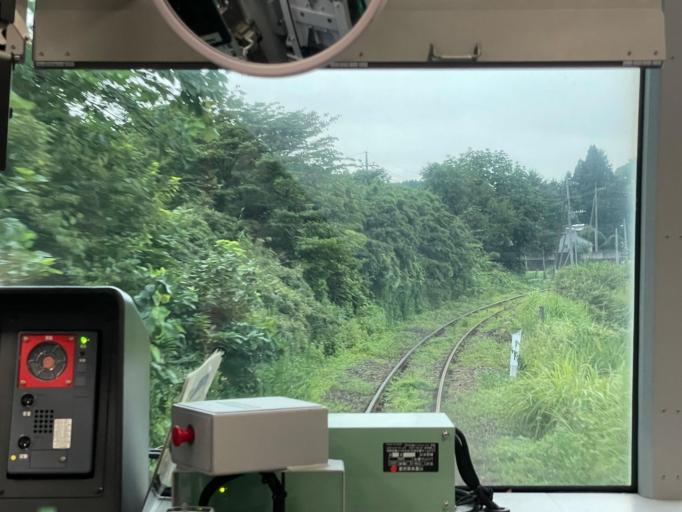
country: JP
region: Tochigi
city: Karasuyama
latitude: 36.6641
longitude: 140.0811
